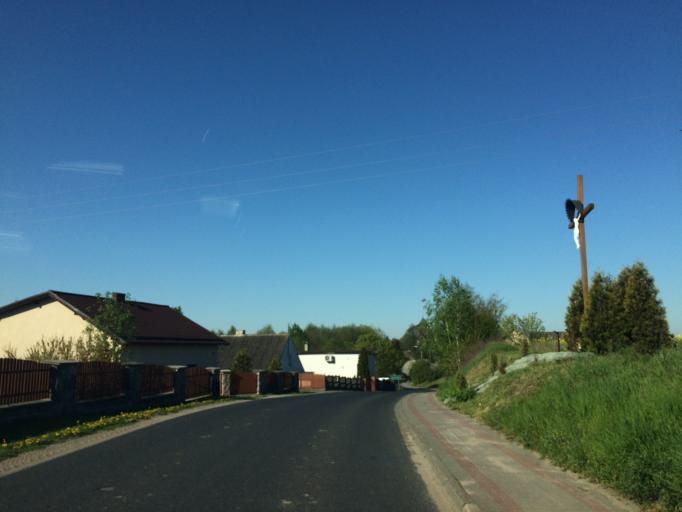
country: PL
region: Warmian-Masurian Voivodeship
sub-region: Powiat ilawski
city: Lubawa
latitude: 53.4153
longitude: 19.7653
